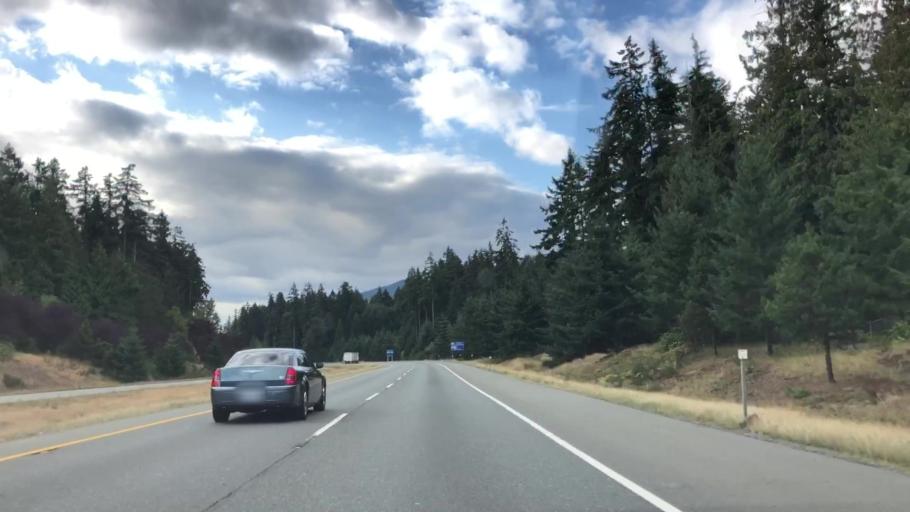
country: CA
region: British Columbia
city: Nanaimo
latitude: 49.2129
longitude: -124.0437
